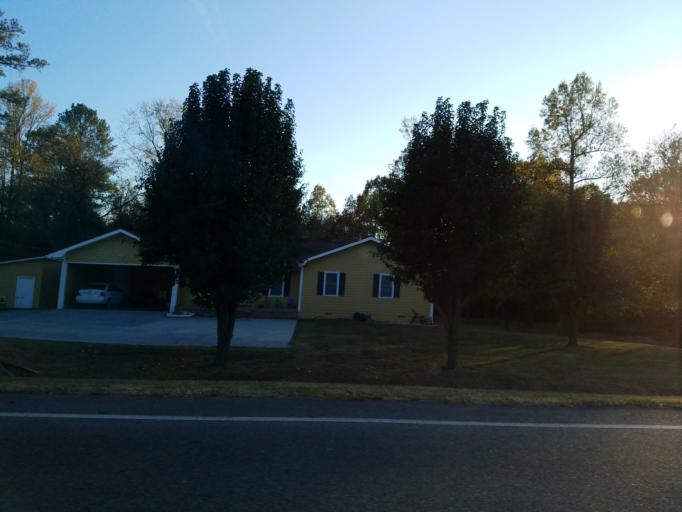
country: US
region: Georgia
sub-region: Gordon County
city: Calhoun
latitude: 34.5177
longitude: -84.9645
